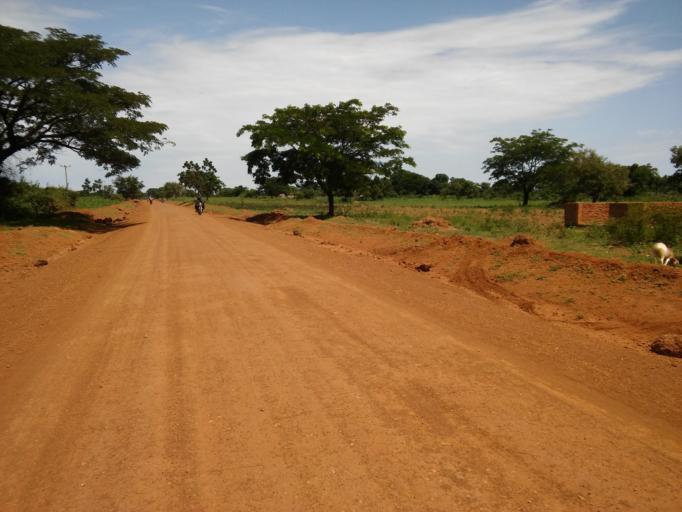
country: UG
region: Eastern Region
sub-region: Kumi District
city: Kumi
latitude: 1.4781
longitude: 33.8867
